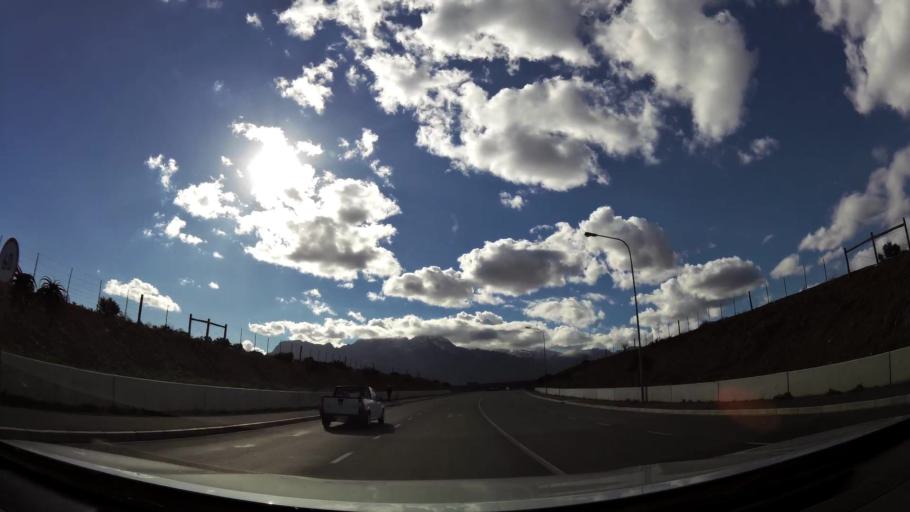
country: ZA
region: Western Cape
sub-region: Cape Winelands District Municipality
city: Worcester
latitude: -33.6339
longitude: 19.4274
